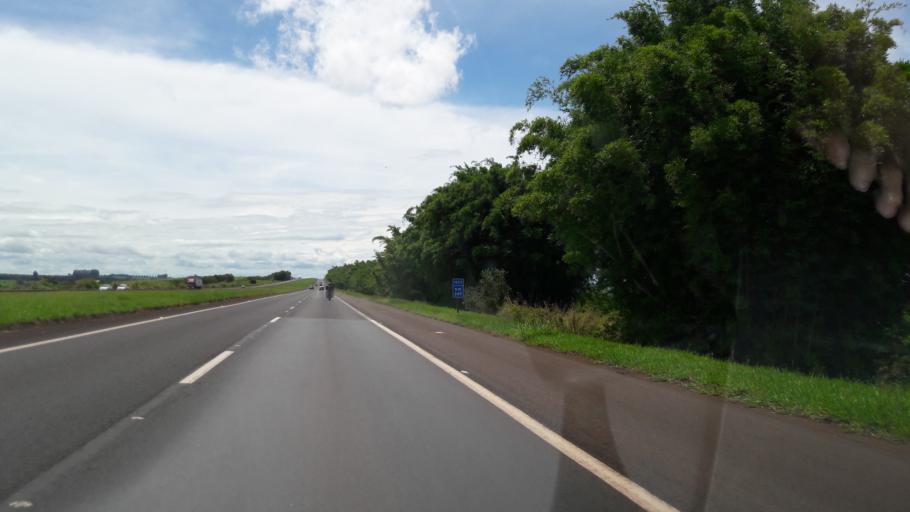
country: BR
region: Sao Paulo
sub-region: Avare
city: Avare
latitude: -22.9511
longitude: -48.8784
